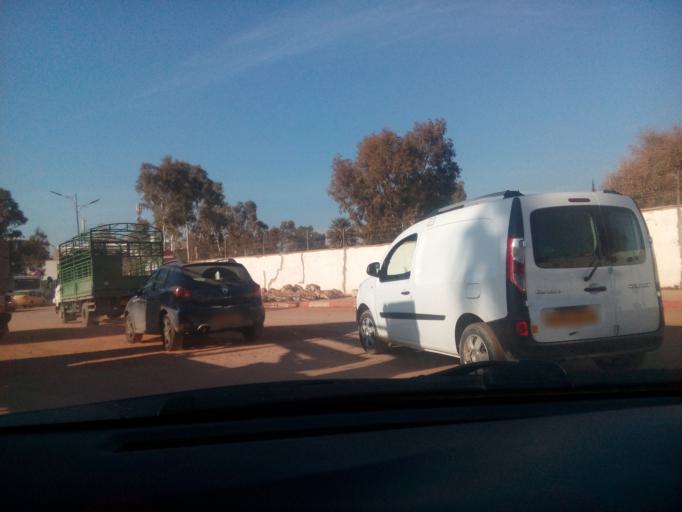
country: DZ
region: Oran
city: Es Senia
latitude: 35.6493
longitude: -0.6116
